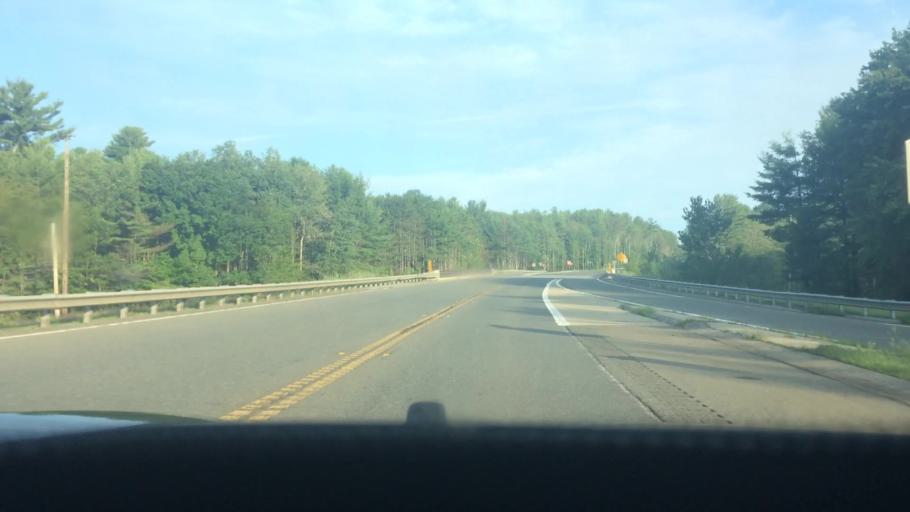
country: US
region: Massachusetts
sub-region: Franklin County
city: Orange
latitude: 42.5581
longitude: -72.3001
